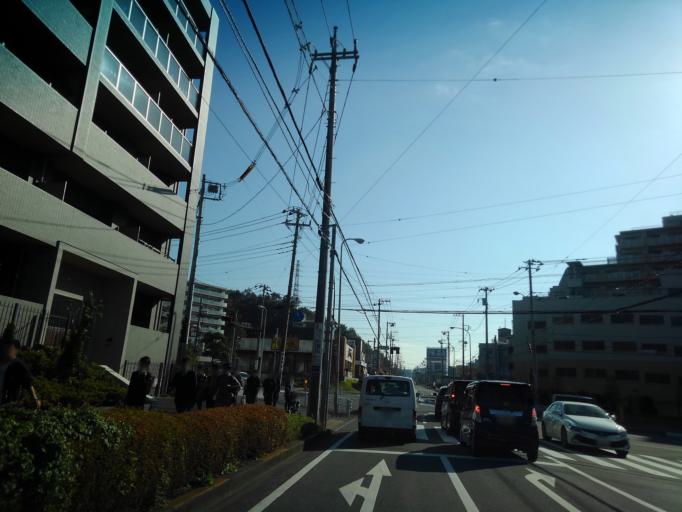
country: JP
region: Tokyo
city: Hachioji
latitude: 35.6031
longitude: 139.3660
